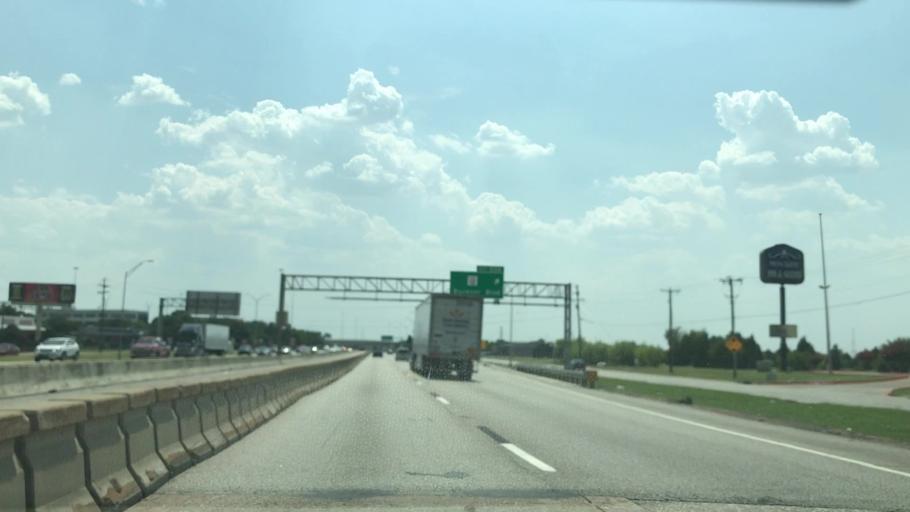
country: US
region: Texas
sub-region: Dallas County
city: Mesquite
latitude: 32.8035
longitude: -96.6690
